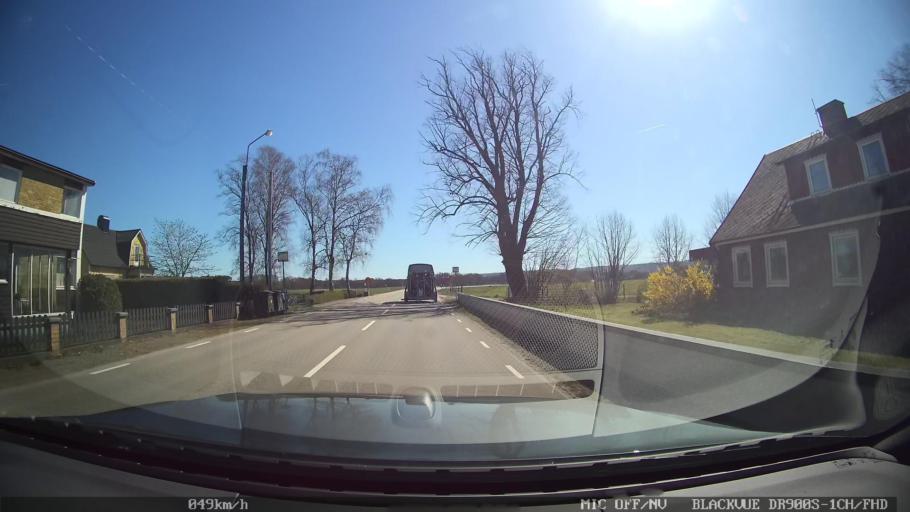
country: SE
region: Skane
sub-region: Klippans Kommun
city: Klippan
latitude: 56.1159
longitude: 13.1795
